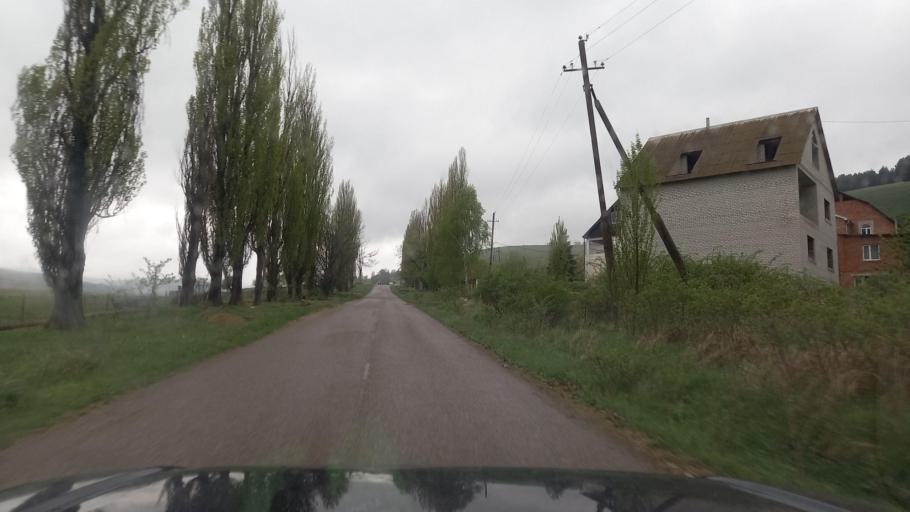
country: RU
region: Stavropol'skiy
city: Nezhinskiy
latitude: 43.8756
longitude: 42.6747
